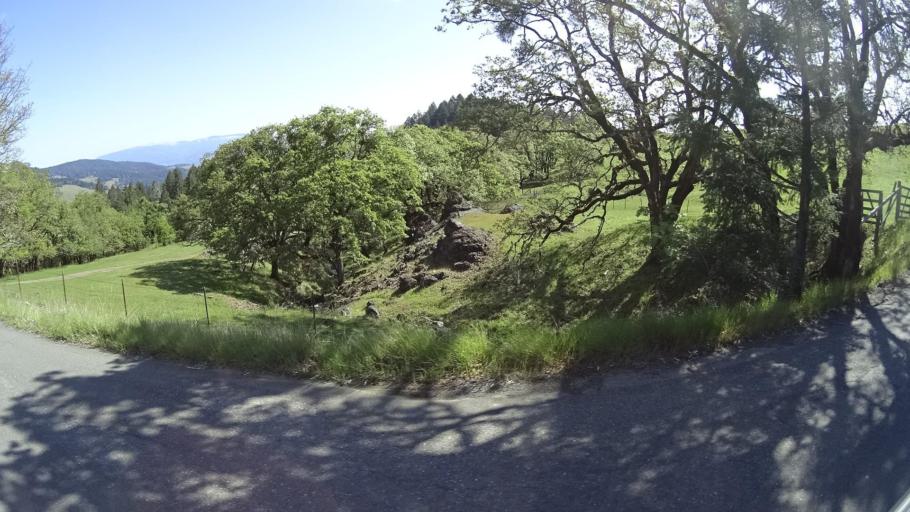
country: US
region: California
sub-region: Humboldt County
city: Redway
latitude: 40.0824
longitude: -123.6590
